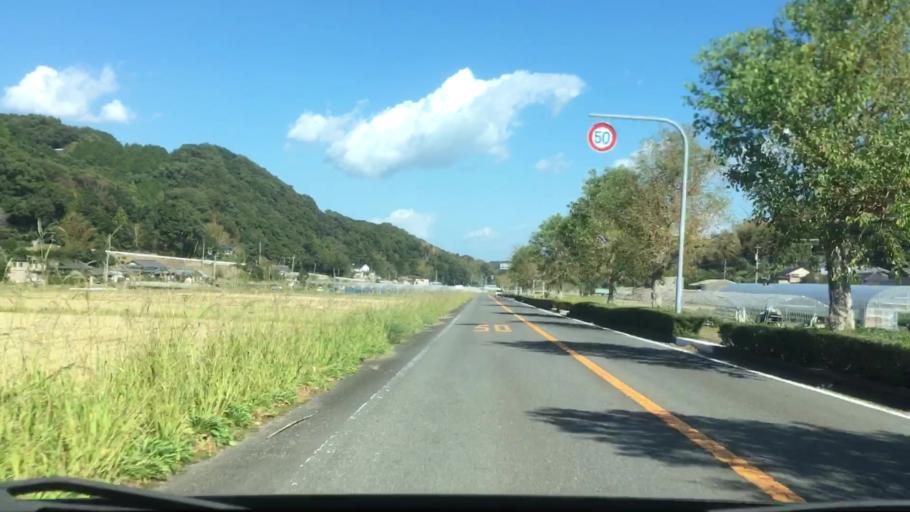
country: JP
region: Nagasaki
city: Sasebo
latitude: 32.9595
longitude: 129.6444
